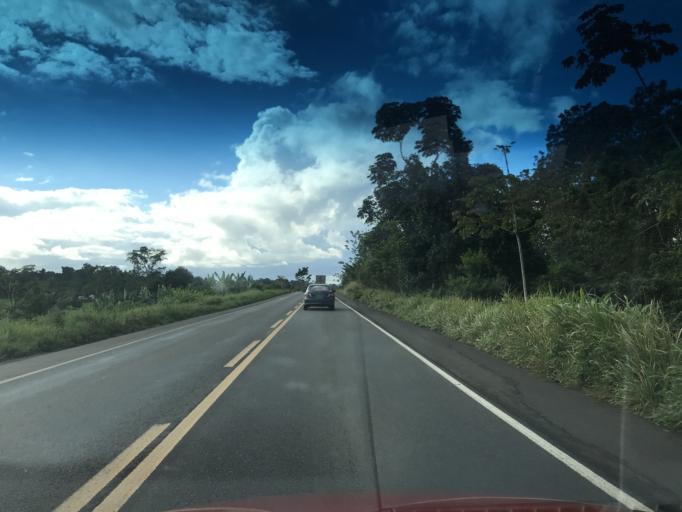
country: BR
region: Bahia
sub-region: Ibirapitanga
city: Ibirapitanga
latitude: -14.1655
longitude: -39.3285
